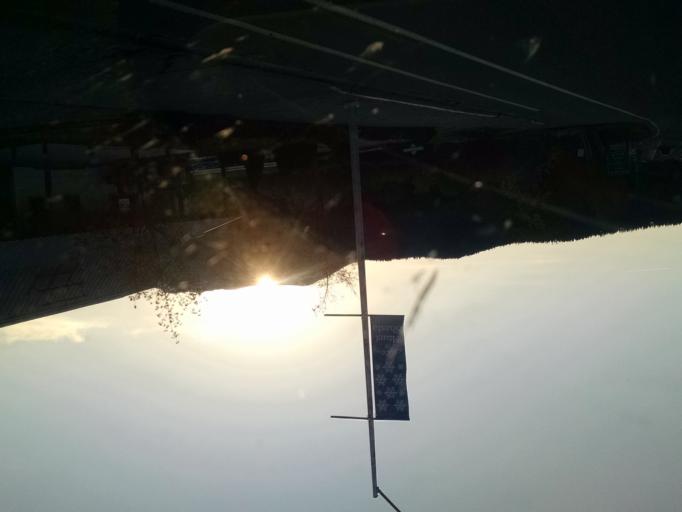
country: US
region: California
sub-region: Siskiyou County
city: Mount Shasta
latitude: 41.3111
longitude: -122.3171
